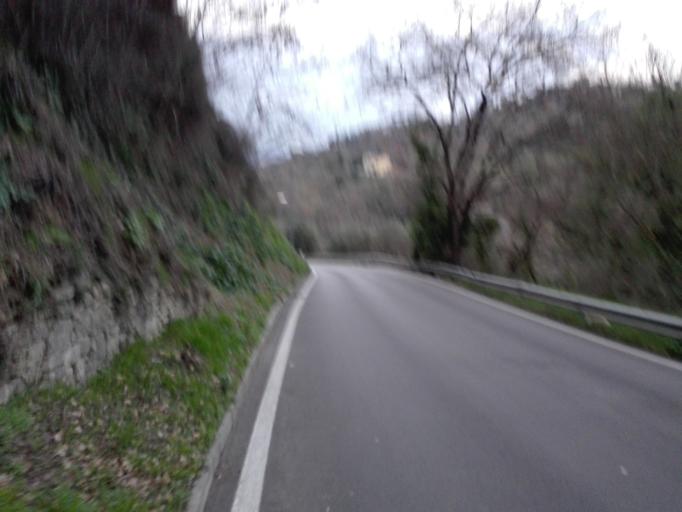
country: IT
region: Umbria
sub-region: Provincia di Perugia
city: Perugia
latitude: 43.1206
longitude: 12.3918
